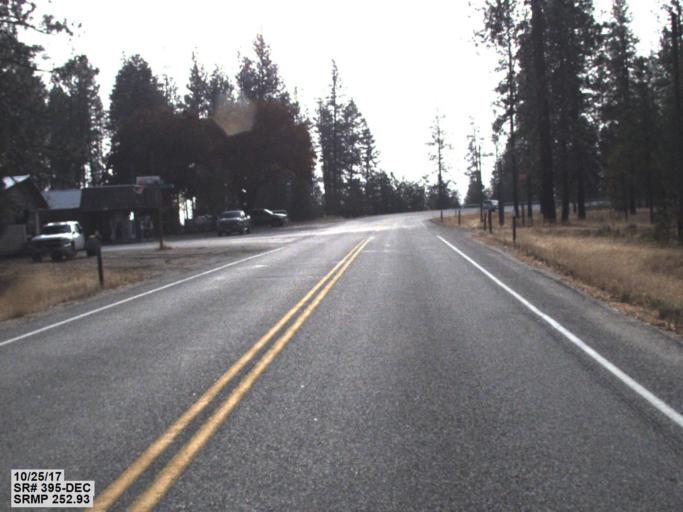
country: US
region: Washington
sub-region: Stevens County
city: Kettle Falls
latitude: 48.7773
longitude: -118.1428
